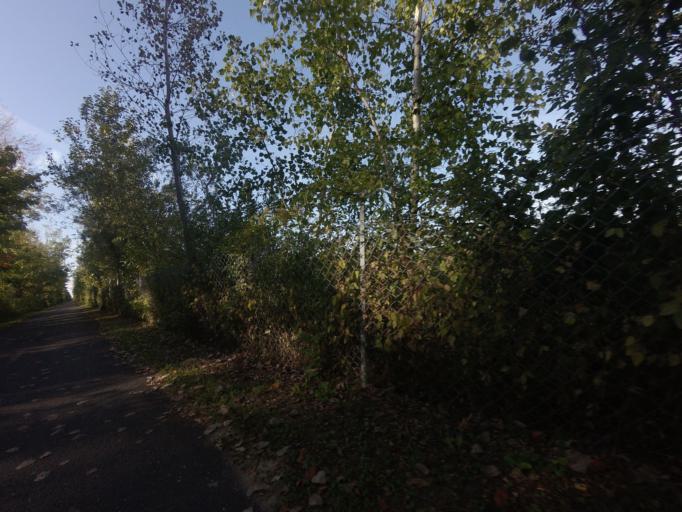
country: CA
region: Quebec
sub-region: Laurentides
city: Blainville
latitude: 45.7273
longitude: -73.9391
